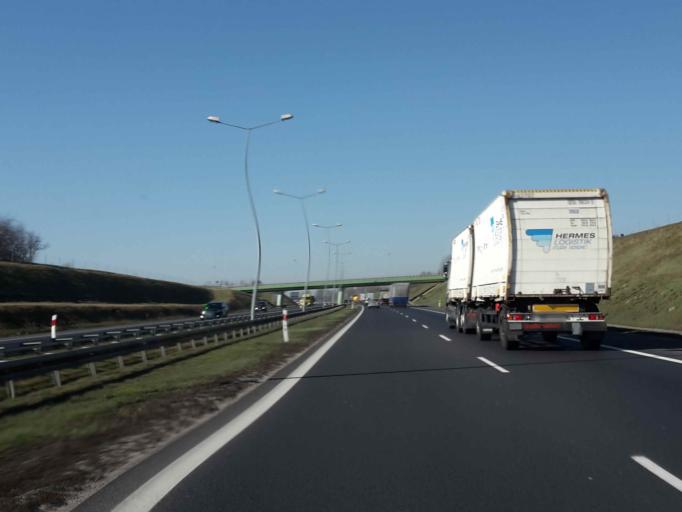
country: PL
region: Greater Poland Voivodeship
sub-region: Powiat poznanski
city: Lubon
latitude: 52.3548
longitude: 16.8877
